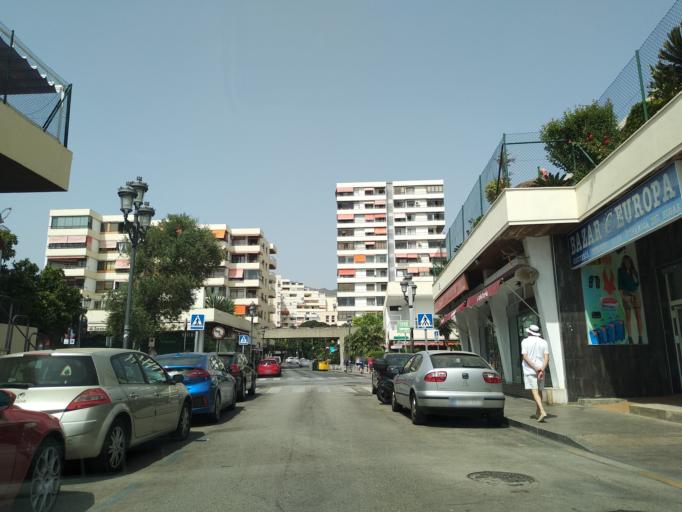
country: ES
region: Andalusia
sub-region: Provincia de Malaga
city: Torremolinos
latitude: 36.6211
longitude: -4.4980
